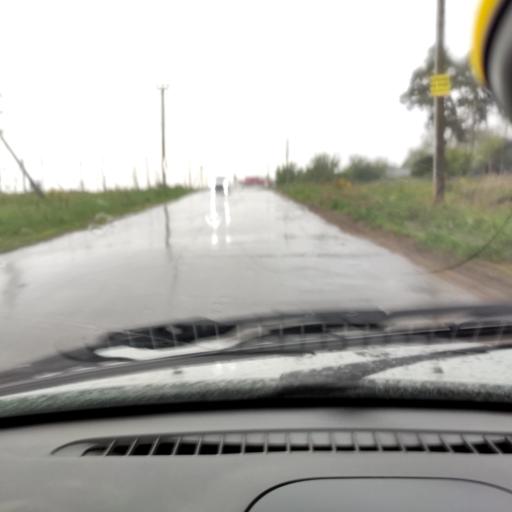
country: RU
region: Samara
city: Zhigulevsk
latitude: 53.5562
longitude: 49.5388
